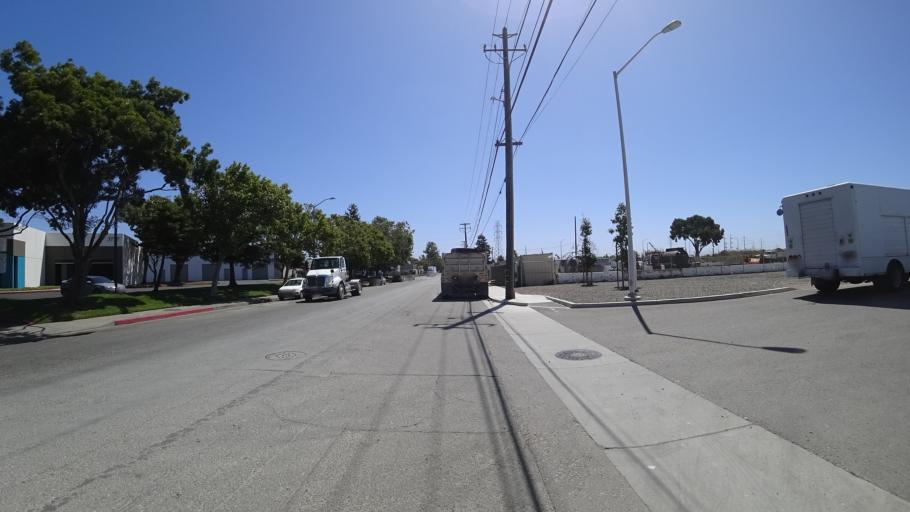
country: US
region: California
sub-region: Alameda County
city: San Lorenzo
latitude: 37.6378
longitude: -122.1343
